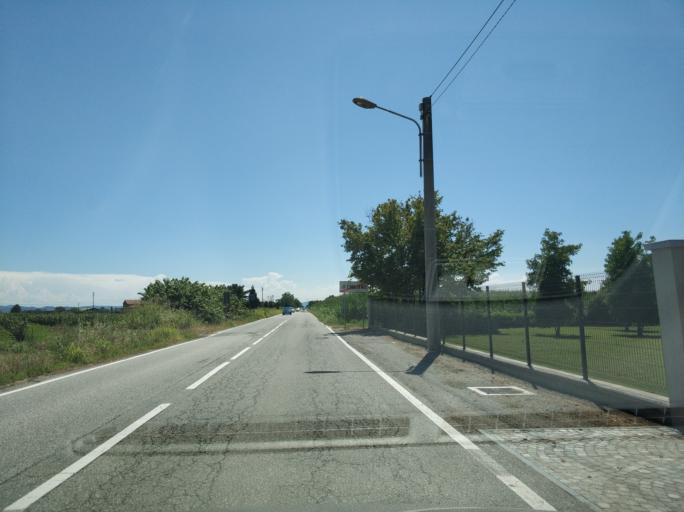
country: IT
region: Piedmont
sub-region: Provincia di Vercelli
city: Cigliano
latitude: 45.3033
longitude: 8.0118
